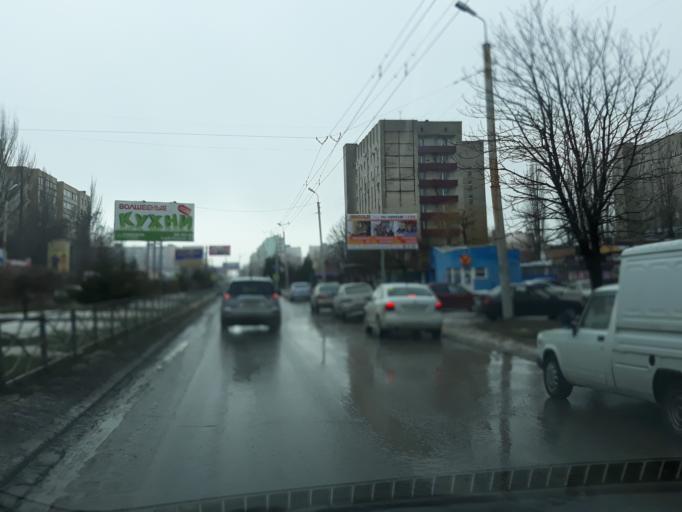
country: RU
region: Rostov
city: Taganrog
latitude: 47.2204
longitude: 38.8648
